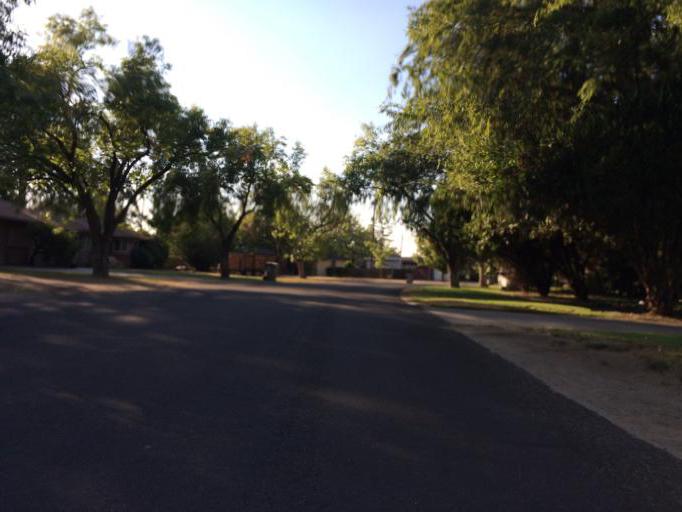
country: US
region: California
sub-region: Fresno County
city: Tarpey Village
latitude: 36.8002
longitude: -119.7040
